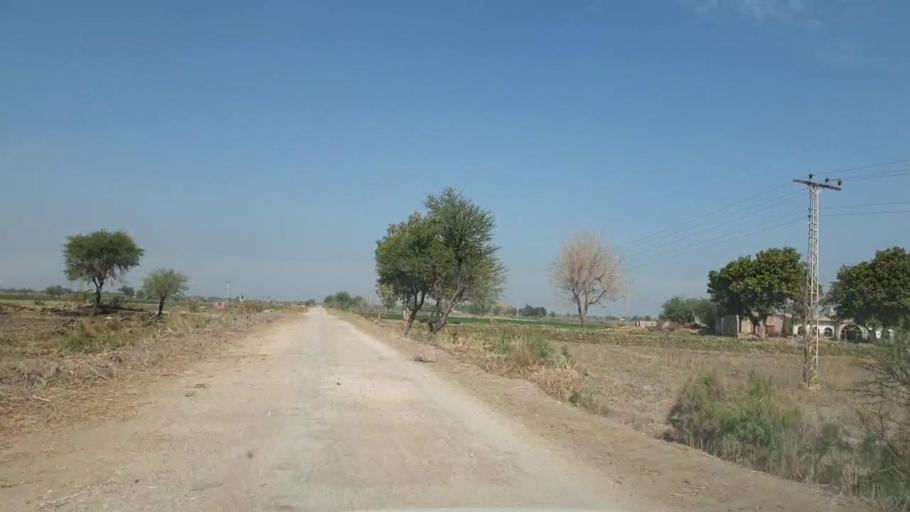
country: PK
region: Sindh
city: Pithoro
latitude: 25.5650
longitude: 69.2073
